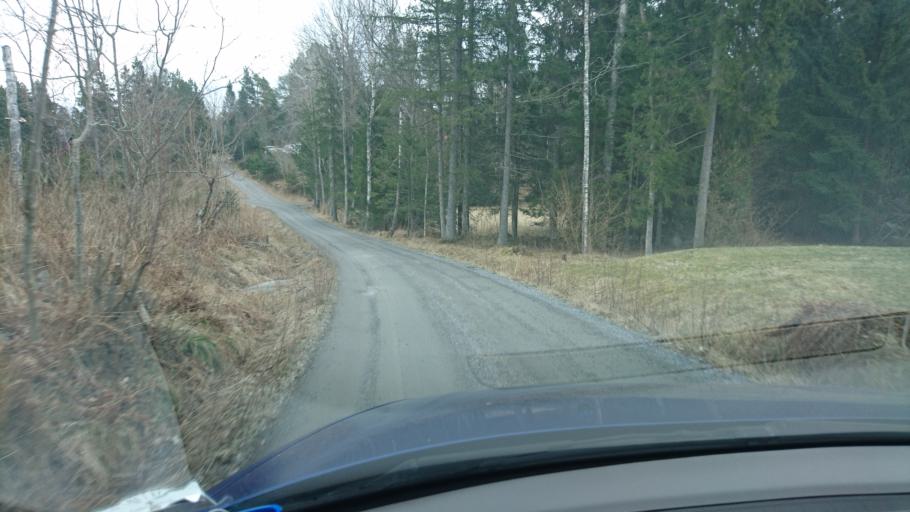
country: SE
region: Stockholm
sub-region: Norrtalje Kommun
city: Bjorko
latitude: 59.7901
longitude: 18.9901
